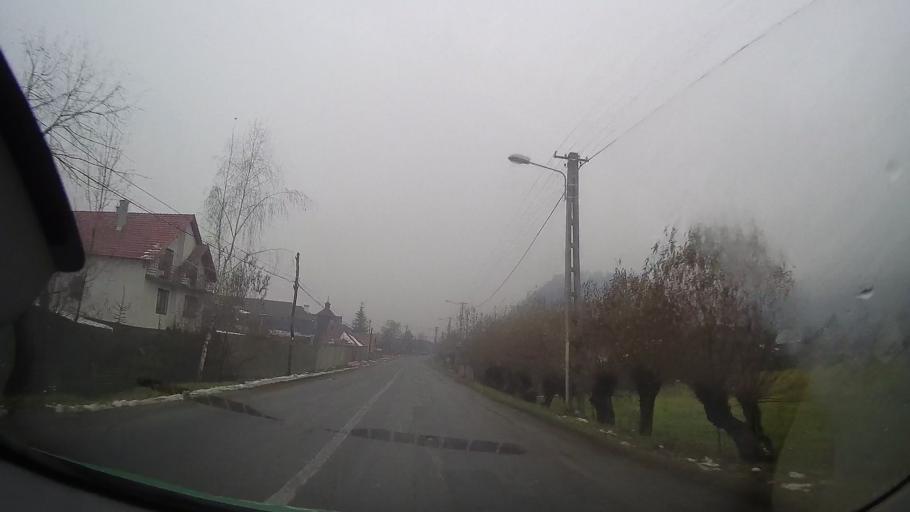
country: RO
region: Harghita
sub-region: Municipiul Gheorgheni
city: Gheorgheni
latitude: 46.7269
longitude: 25.6308
